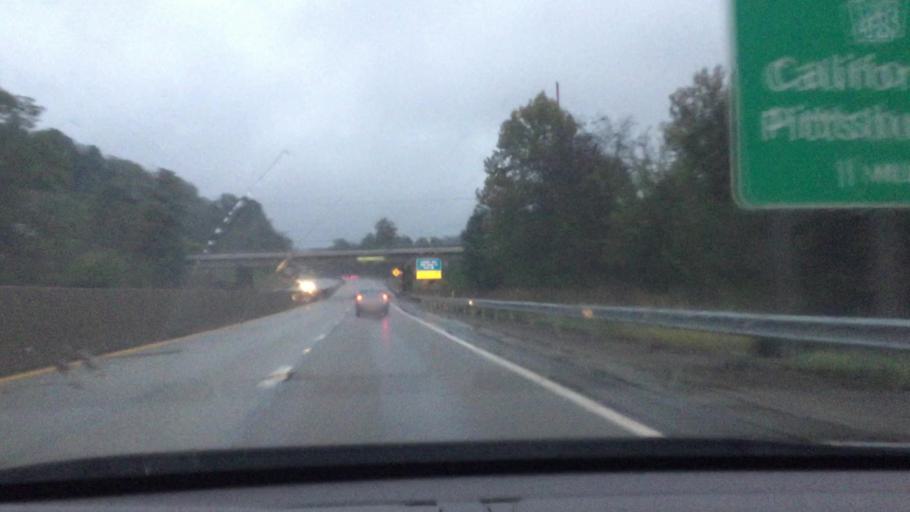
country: US
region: Pennsylvania
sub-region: Washington County
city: Charleroi
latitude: 40.1148
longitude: -79.9425
